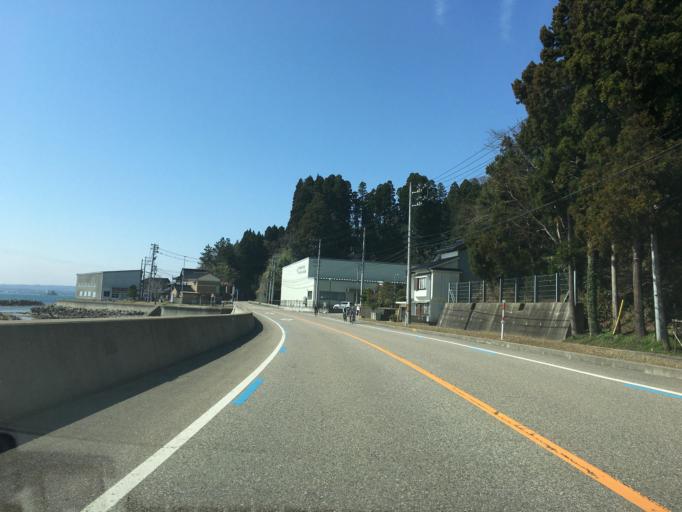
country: JP
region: Toyama
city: Himi
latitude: 36.8930
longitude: 137.0051
